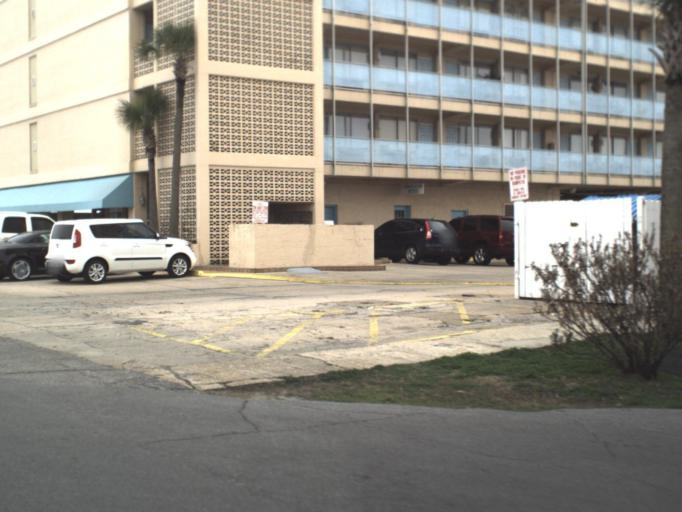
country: US
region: Florida
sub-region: Bay County
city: Panama City Beach
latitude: 30.2040
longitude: -85.8548
